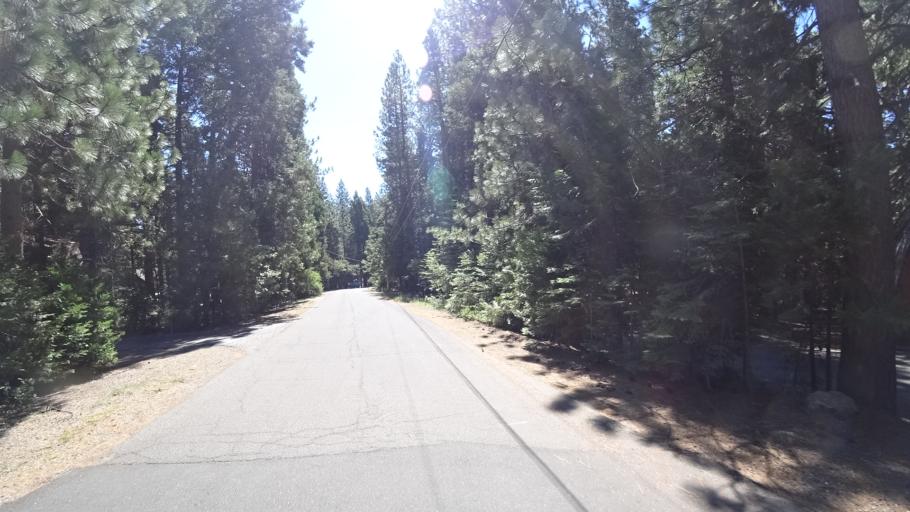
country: US
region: California
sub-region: Calaveras County
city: Arnold
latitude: 38.2840
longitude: -120.2796
